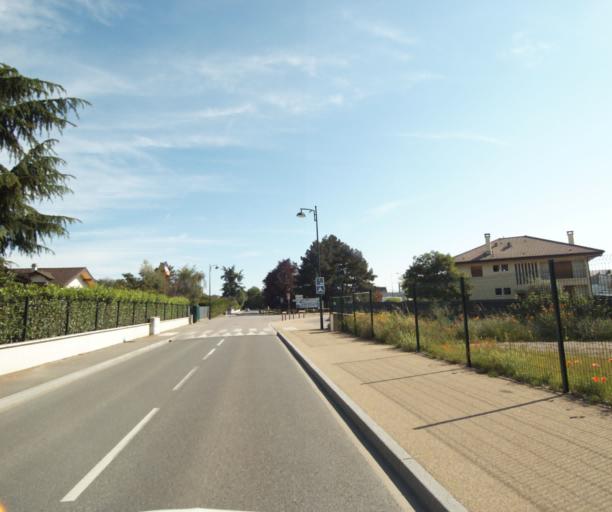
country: FR
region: Rhone-Alpes
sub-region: Departement de la Haute-Savoie
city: Thonon-les-Bains
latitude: 46.3884
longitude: 6.5023
